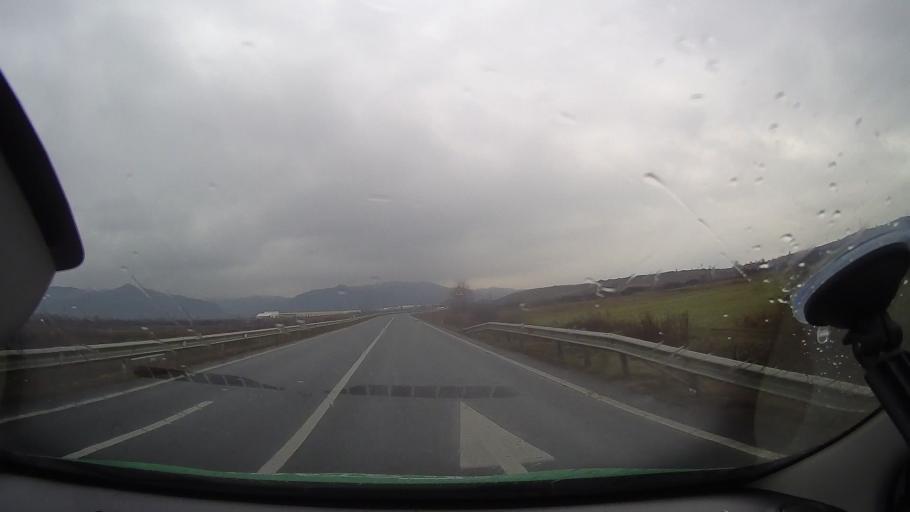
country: RO
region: Hunedoara
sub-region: Comuna Ribita
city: Ribita
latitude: 46.1675
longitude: 22.7460
